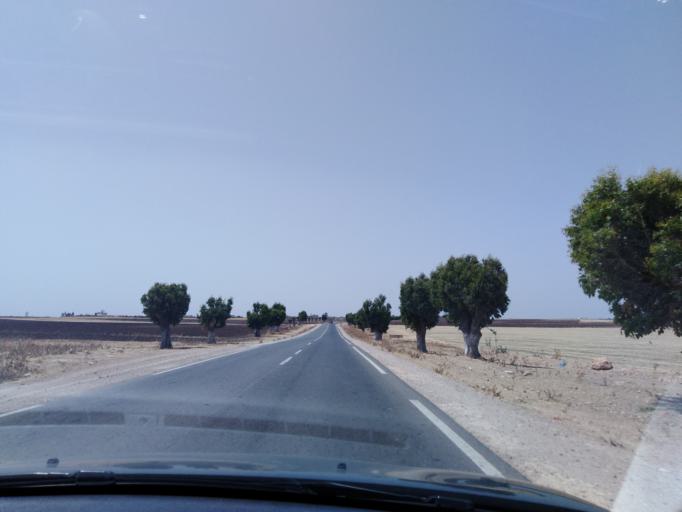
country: MA
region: Doukkala-Abda
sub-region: Safi
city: Youssoufia
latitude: 32.3829
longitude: -8.8255
